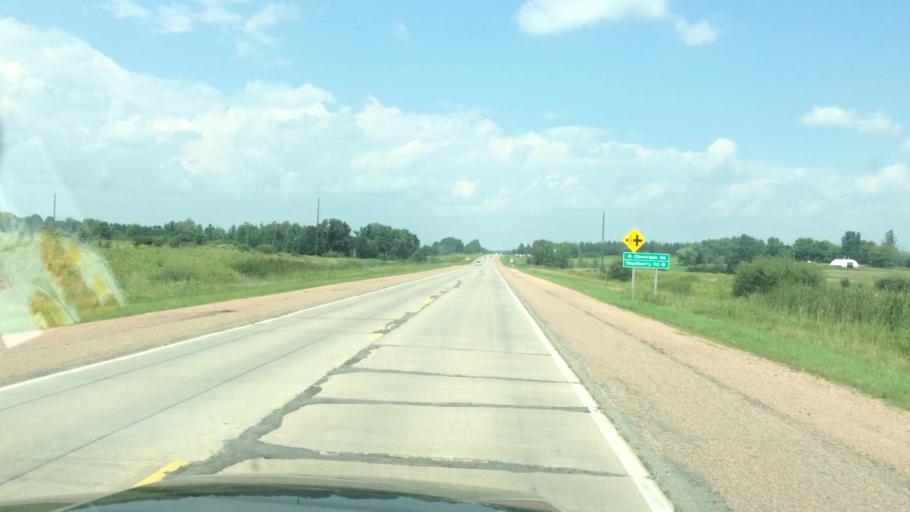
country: US
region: Wisconsin
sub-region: Clark County
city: Colby
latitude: 44.8712
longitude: -90.3157
